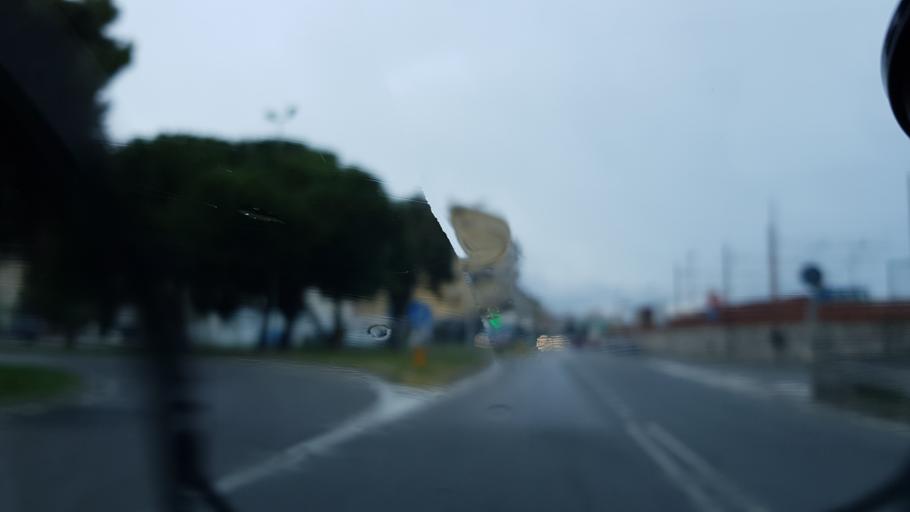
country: IT
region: Liguria
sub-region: Provincia di Savona
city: Valleggia
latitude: 44.2935
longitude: 8.4531
